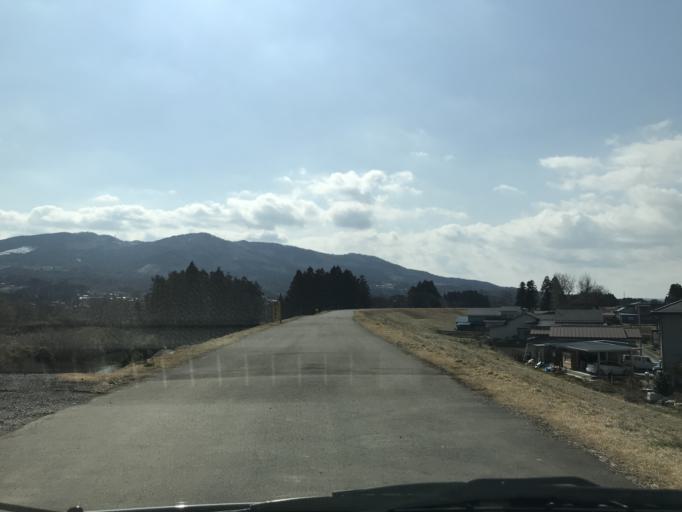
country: JP
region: Iwate
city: Mizusawa
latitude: 39.0491
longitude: 141.1470
